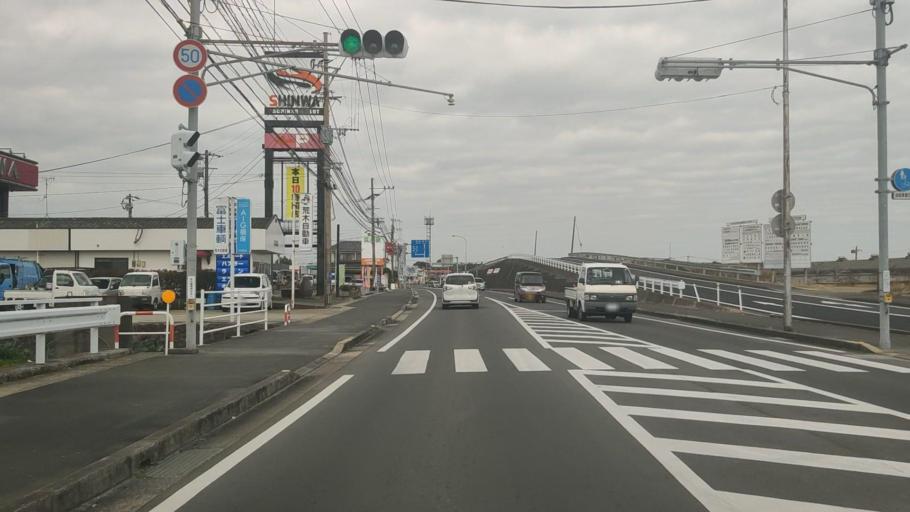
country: JP
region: Nagasaki
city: Shimabara
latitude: 32.8108
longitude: 130.3594
